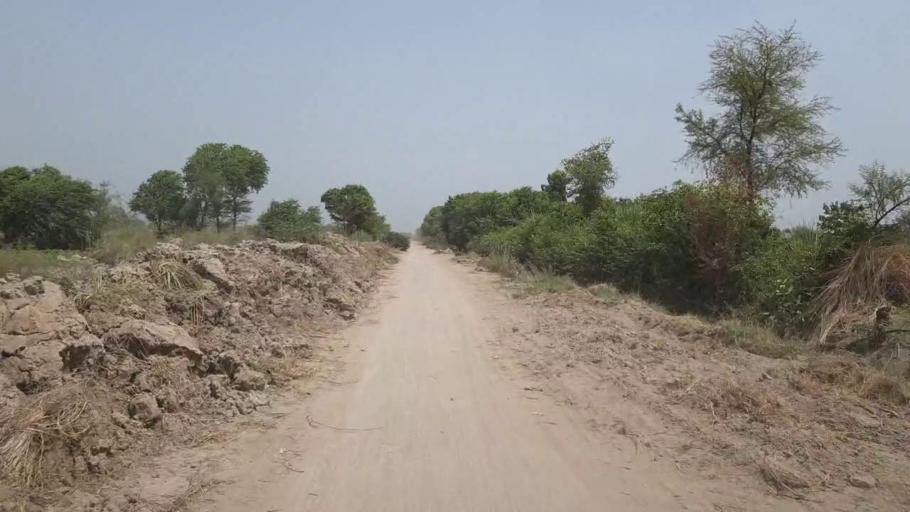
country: PK
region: Sindh
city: Nawabshah
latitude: 26.3188
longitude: 68.2986
